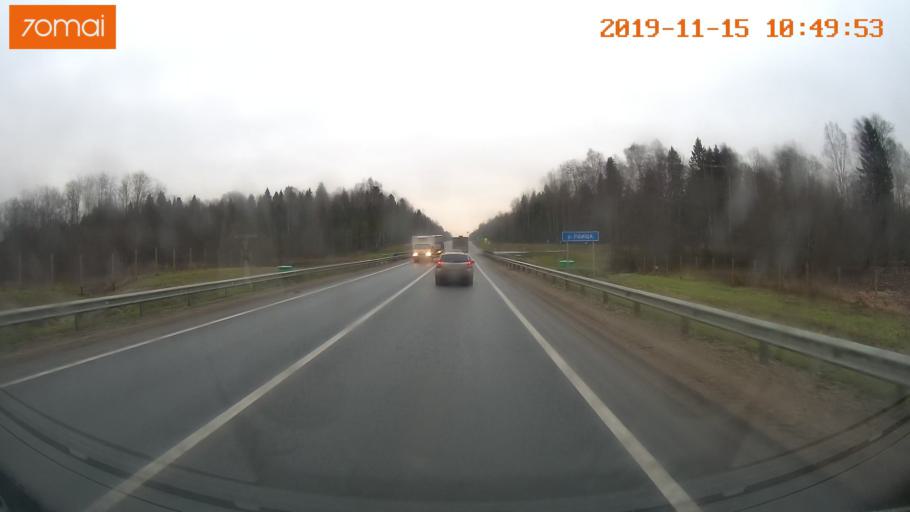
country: RU
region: Vologda
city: Sheksna
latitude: 59.1879
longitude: 38.6695
